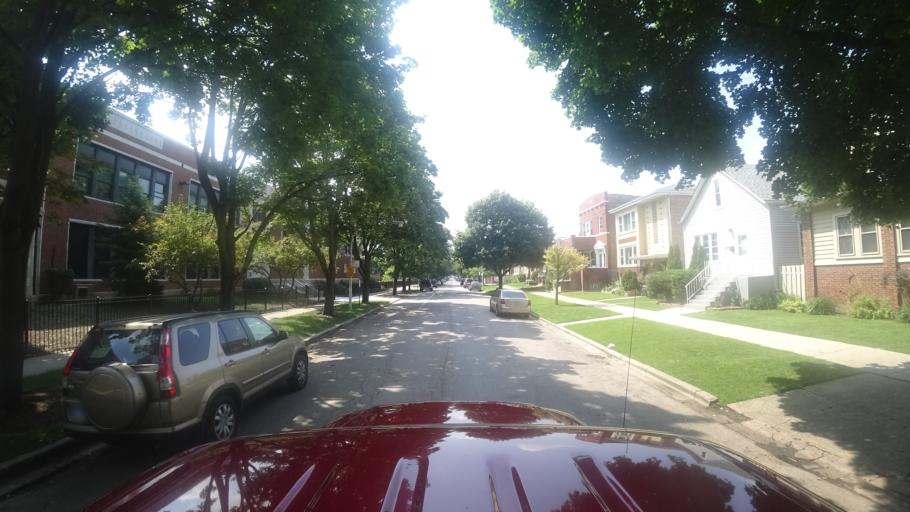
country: US
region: Illinois
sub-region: Cook County
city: Cicero
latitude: 41.8055
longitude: -87.7260
